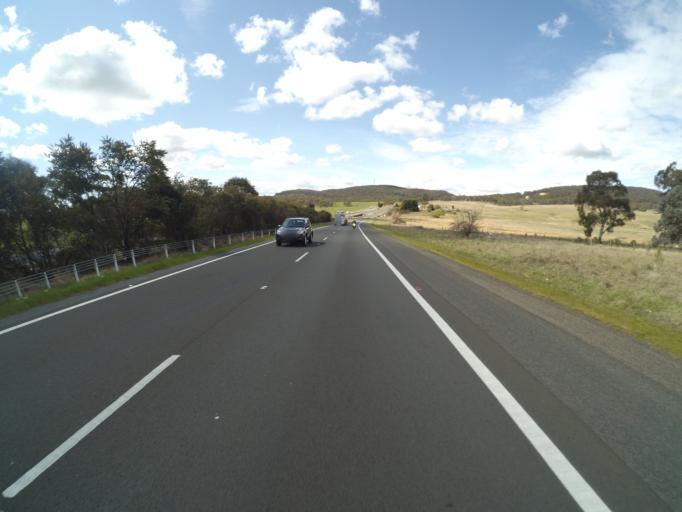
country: AU
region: New South Wales
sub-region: Goulburn Mulwaree
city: Goulburn
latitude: -34.7418
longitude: 149.9080
